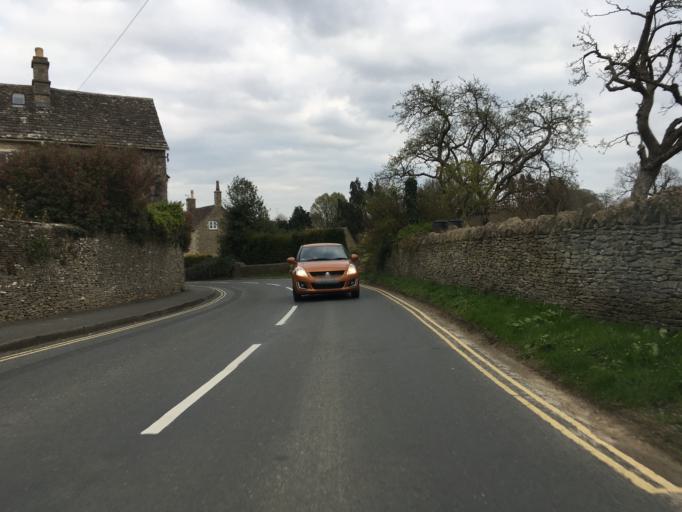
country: GB
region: England
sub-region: Gloucestershire
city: Northleach
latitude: 51.7586
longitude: -1.8408
